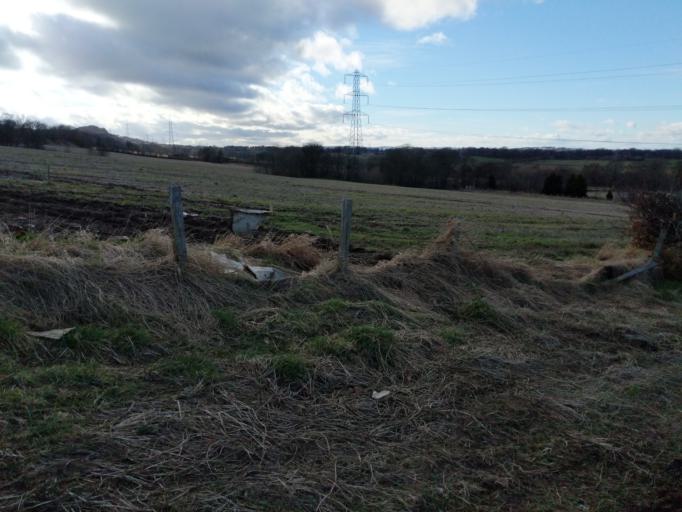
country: GB
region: Scotland
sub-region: Edinburgh
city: Balerno
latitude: 55.8942
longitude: -3.3382
